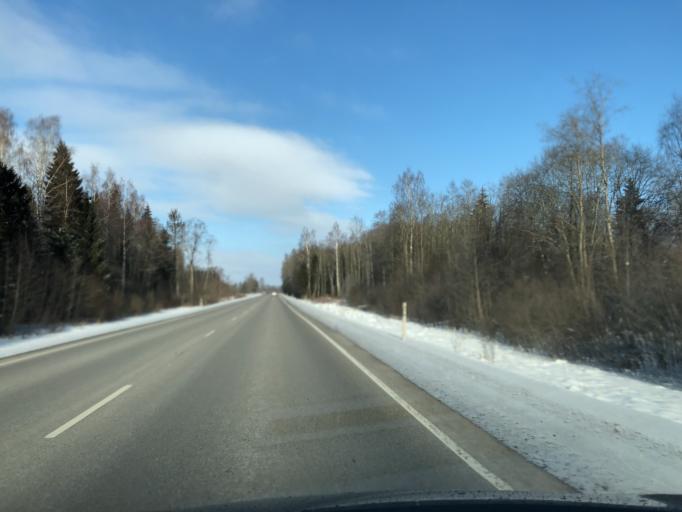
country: EE
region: Jaervamaa
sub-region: Paide linn
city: Paide
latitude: 58.8095
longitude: 25.7577
